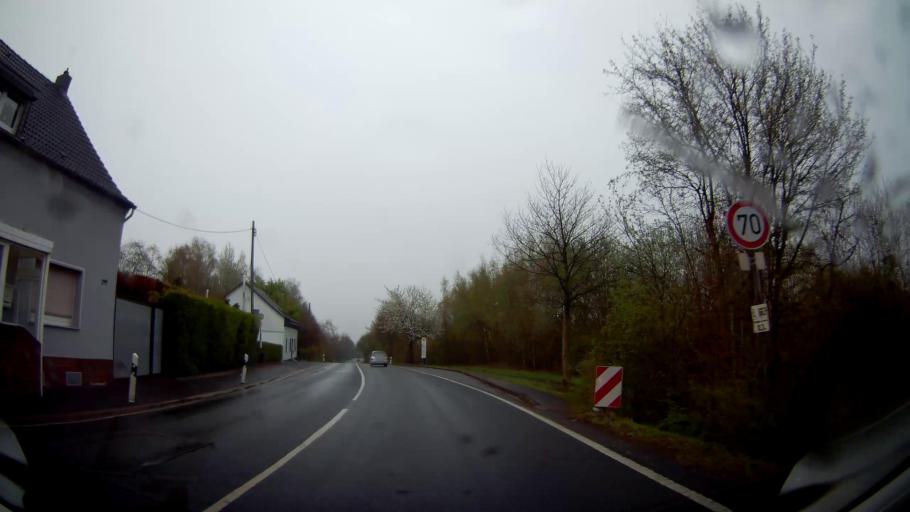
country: DE
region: North Rhine-Westphalia
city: Castrop-Rauxel
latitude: 51.5347
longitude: 7.3418
